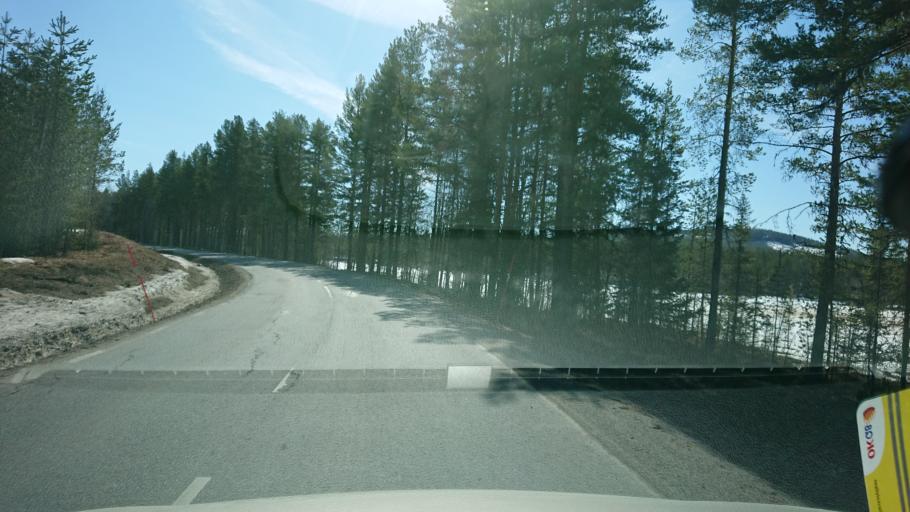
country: SE
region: Vaesterbotten
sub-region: Dorotea Kommun
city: Dorotea
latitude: 64.0098
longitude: 16.2951
